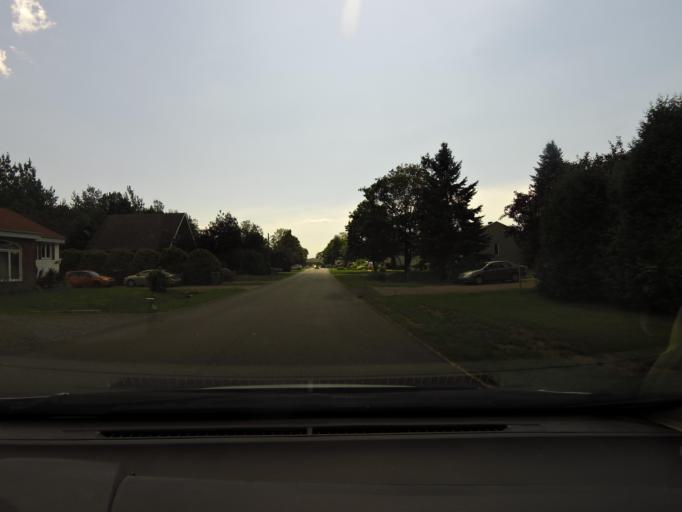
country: CA
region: Quebec
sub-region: Capitale-Nationale
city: Neuville
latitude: 46.7177
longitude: -71.5450
